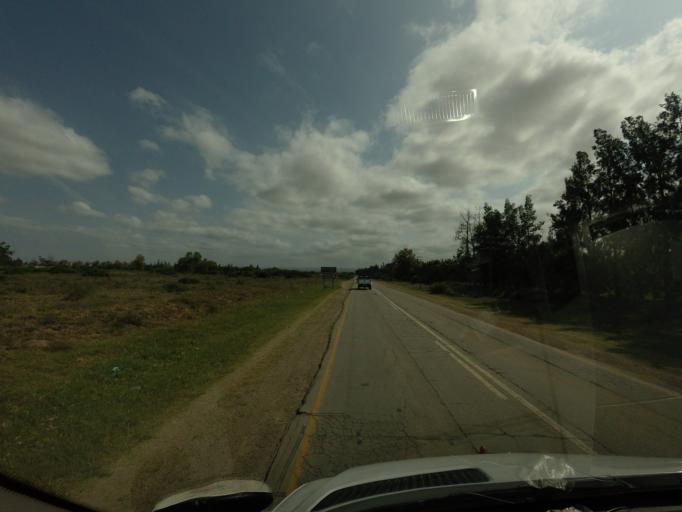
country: ZA
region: Eastern Cape
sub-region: Cacadu District Municipality
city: Kirkwood
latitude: -33.5383
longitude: 25.6906
